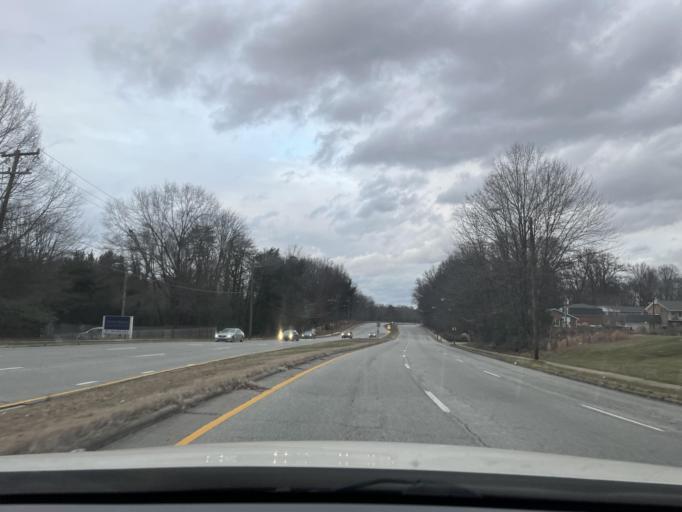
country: US
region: North Carolina
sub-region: Guilford County
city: Greensboro
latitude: 36.0417
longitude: -79.8503
